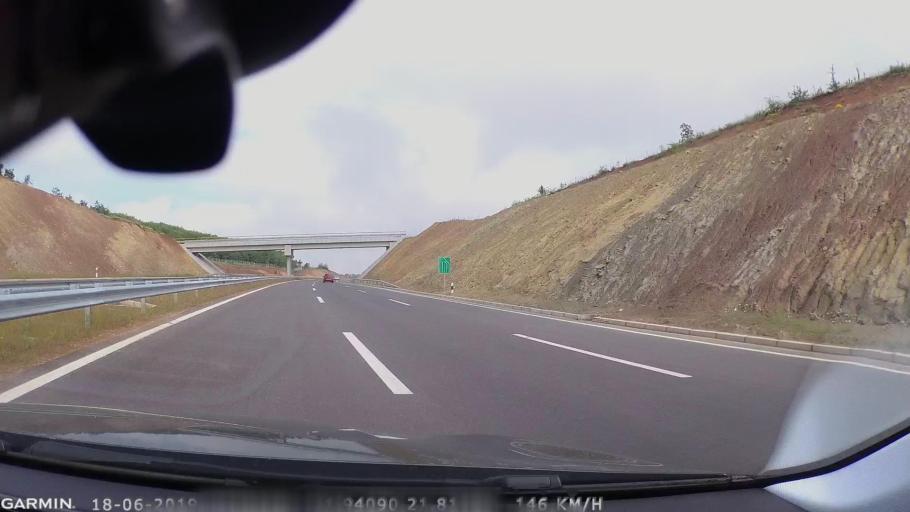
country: MK
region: Sveti Nikole
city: Gorobinci
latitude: 41.9200
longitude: 21.8685
